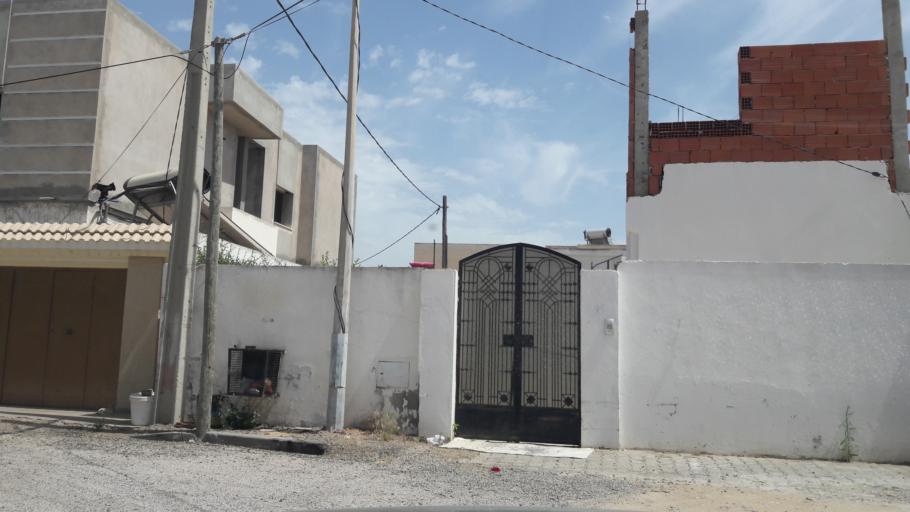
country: TN
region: Safaqis
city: Al Qarmadah
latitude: 34.7757
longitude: 10.7692
